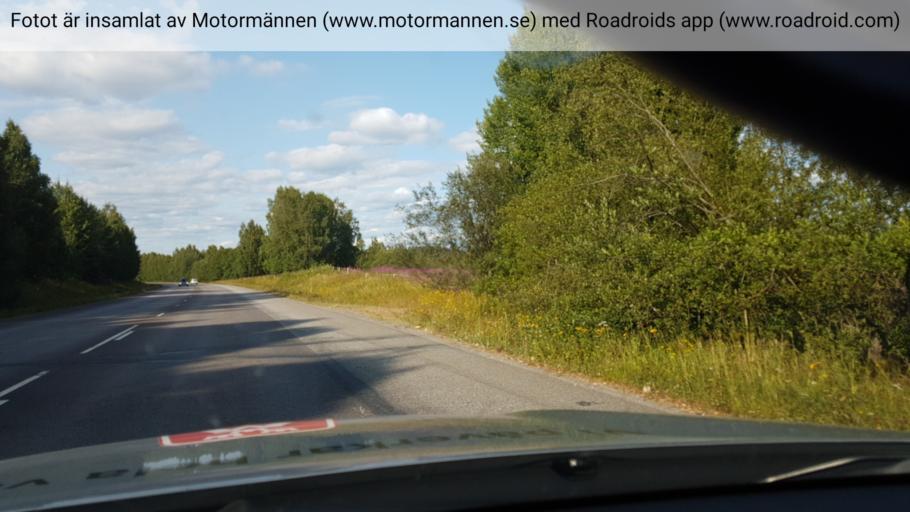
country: SE
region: Norrbotten
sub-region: Pitea Kommun
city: Pitea
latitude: 65.3006
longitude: 21.5105
